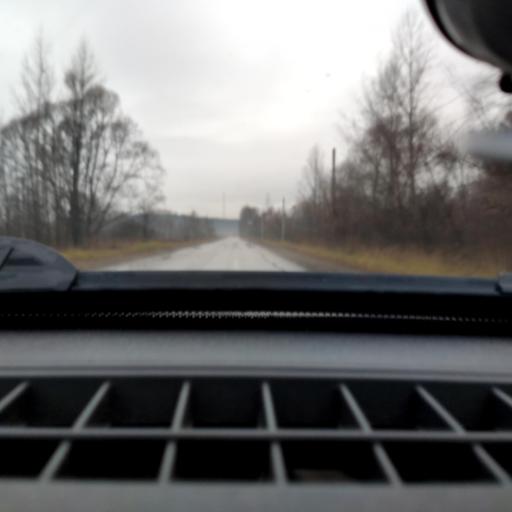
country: RU
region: Bashkortostan
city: Ufa
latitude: 54.8092
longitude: 56.1714
